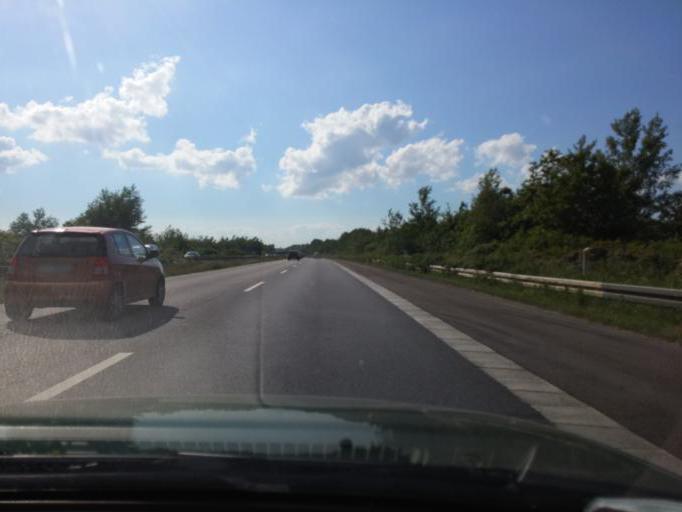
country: DK
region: South Denmark
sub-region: Assens Kommune
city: Vissenbjerg
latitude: 55.4054
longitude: 10.1402
